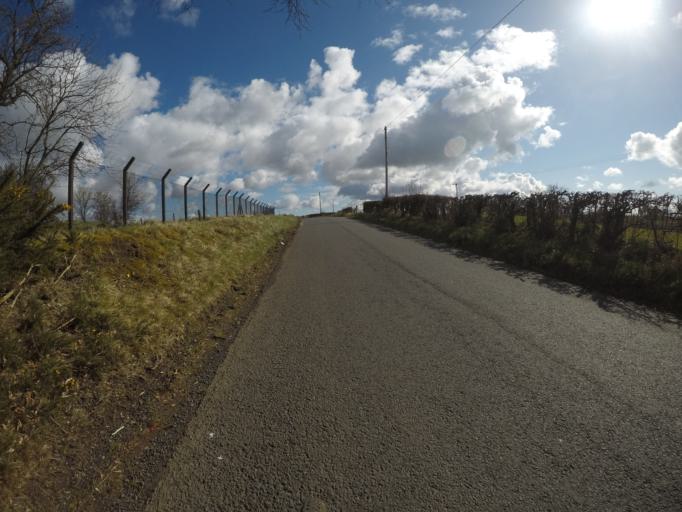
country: GB
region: Scotland
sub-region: North Ayrshire
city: Beith
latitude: 55.7226
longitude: -4.6114
